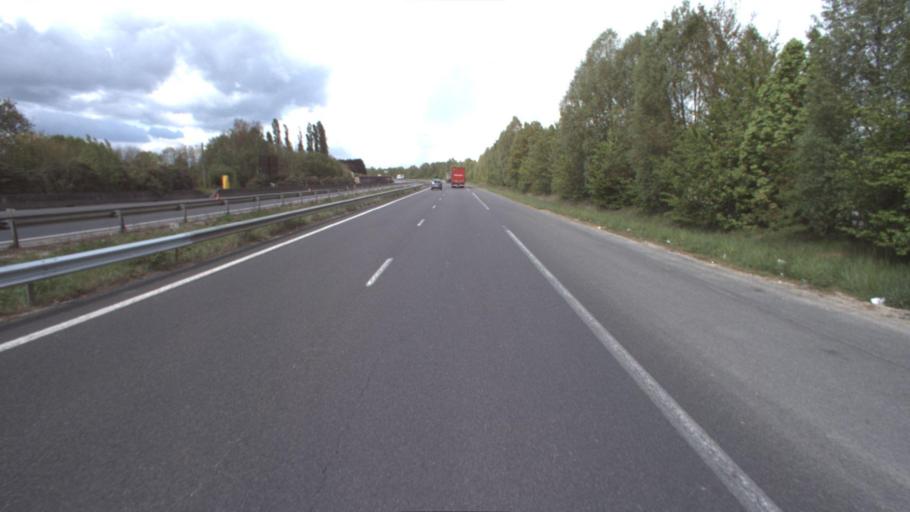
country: FR
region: Ile-de-France
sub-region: Departement de Seine-et-Marne
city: Fontenay-Tresigny
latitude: 48.7068
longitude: 2.8810
